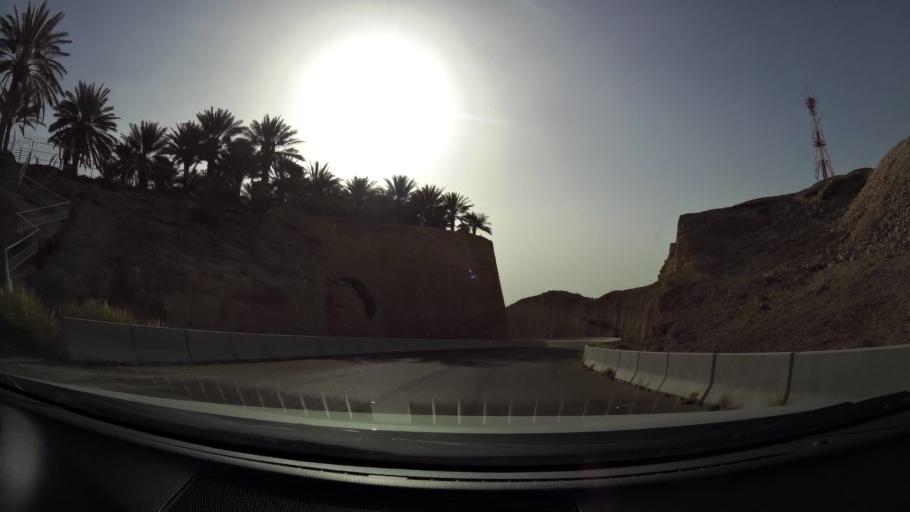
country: AE
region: Abu Dhabi
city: Al Ain
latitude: 24.0772
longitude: 55.7708
